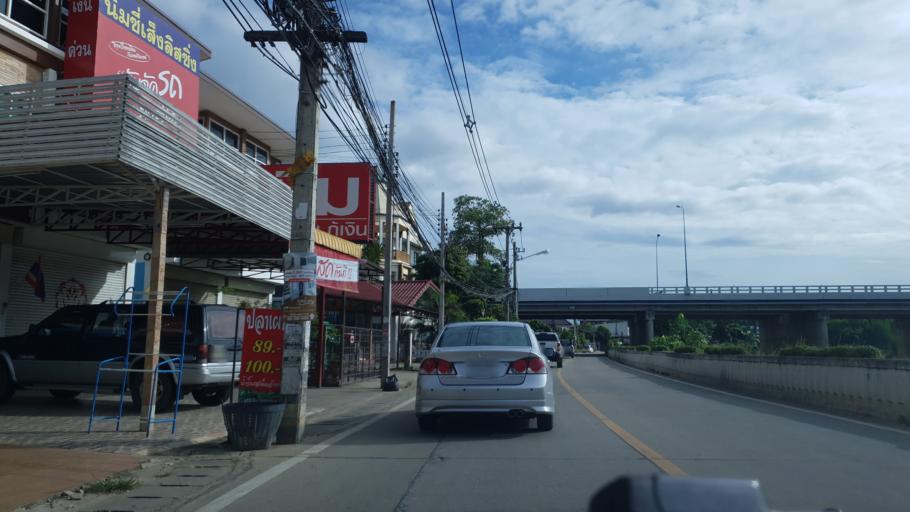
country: TH
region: Chiang Mai
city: Chiang Mai
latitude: 18.7452
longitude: 98.9841
